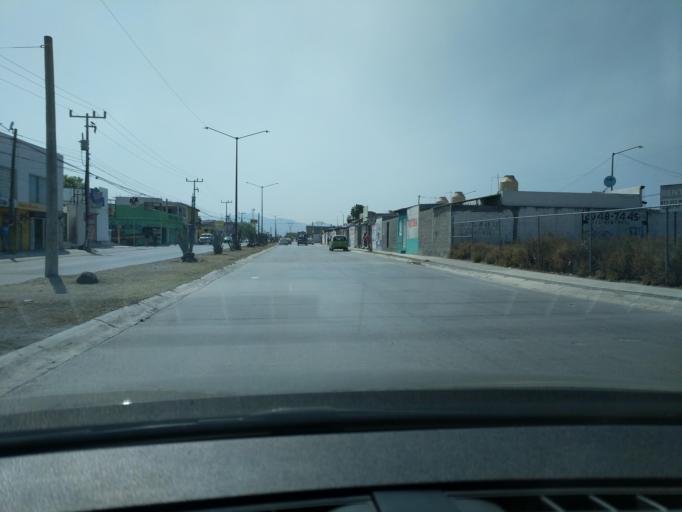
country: MX
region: Nuevo Leon
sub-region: Garcia
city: Valle de Lincoln
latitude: 25.7922
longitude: -100.4805
